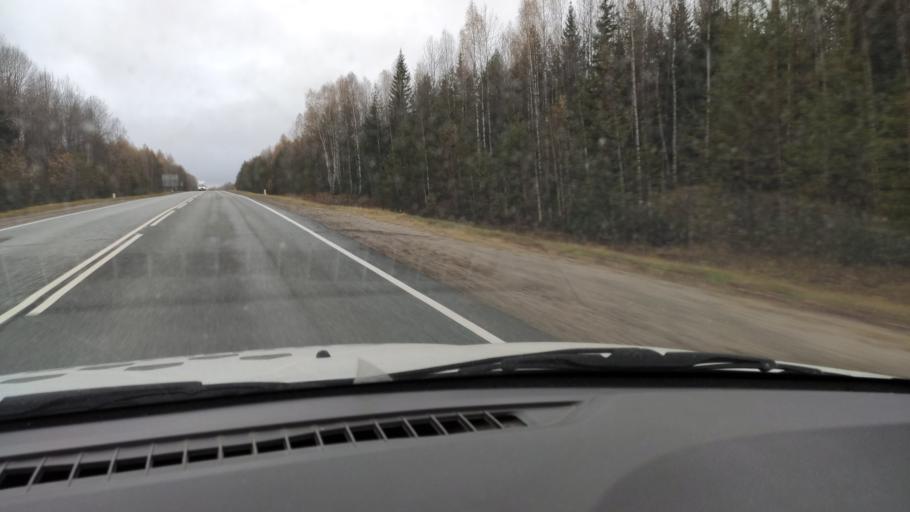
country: RU
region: Kirov
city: Dubrovka
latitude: 58.8942
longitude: 51.3320
